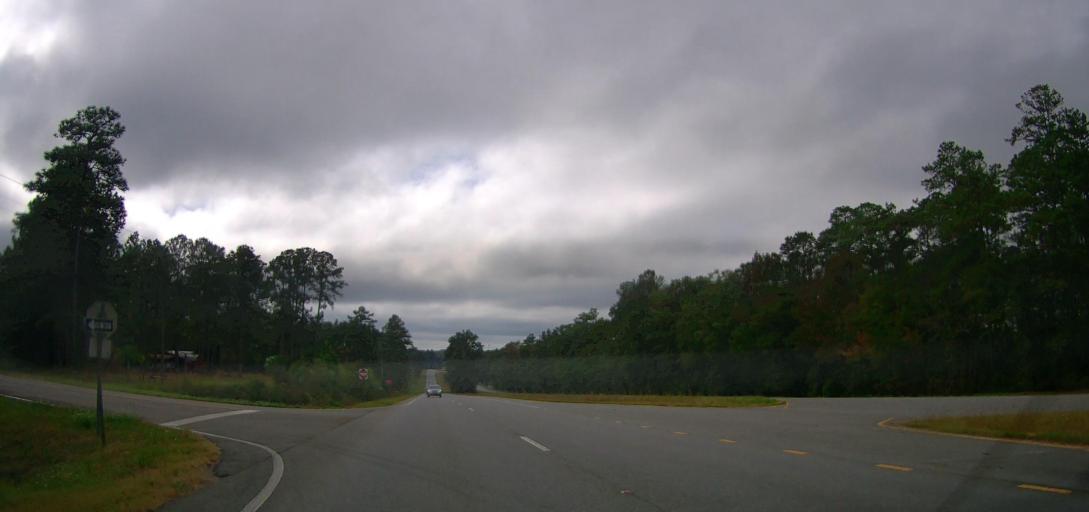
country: US
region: Georgia
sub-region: Grady County
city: Cairo
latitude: 30.7231
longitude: -84.1252
